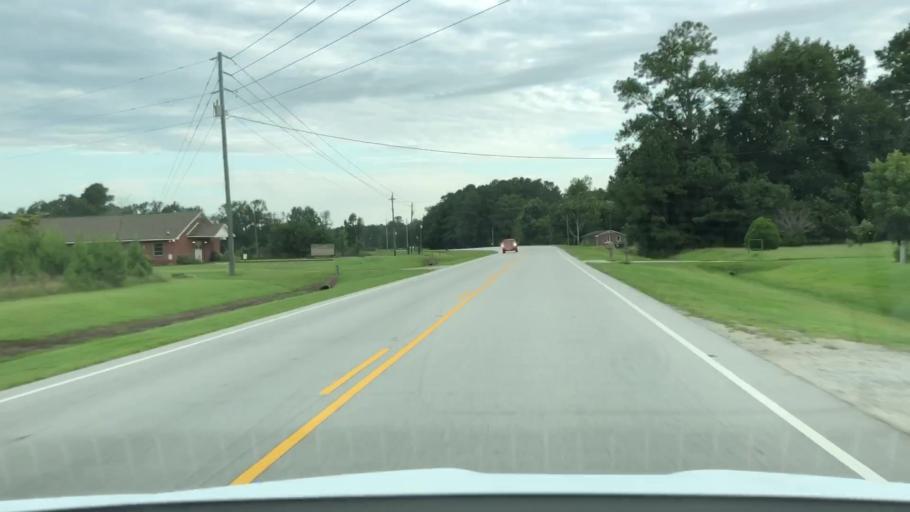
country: US
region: North Carolina
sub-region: Jones County
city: Trenton
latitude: 35.0272
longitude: -77.3089
